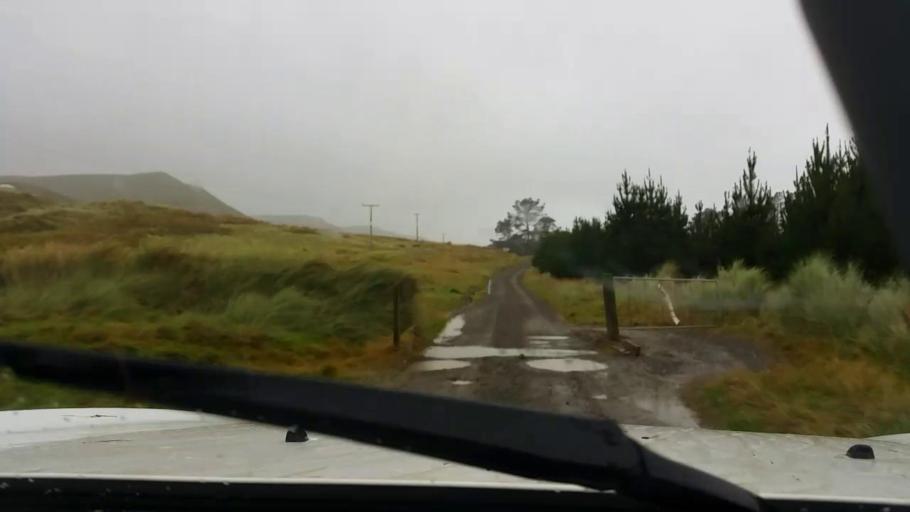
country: NZ
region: Wellington
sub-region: Masterton District
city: Masterton
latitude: -41.2531
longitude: 175.9132
